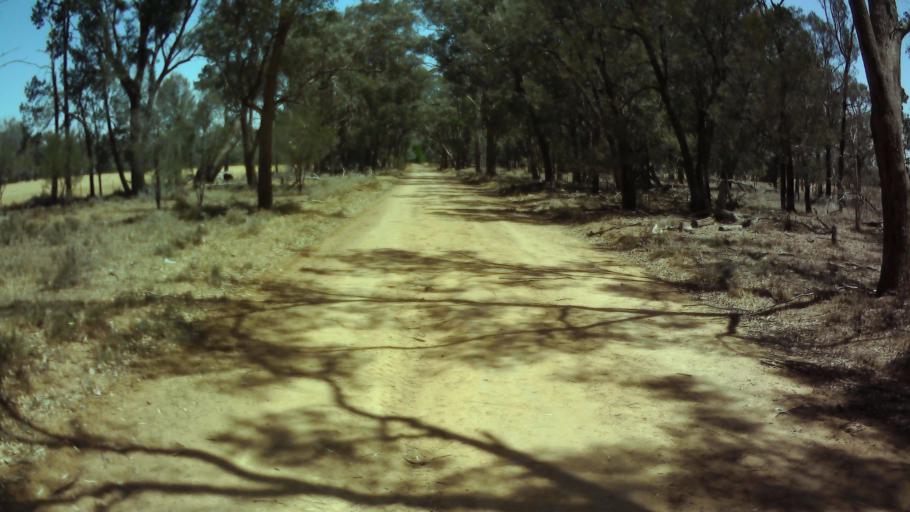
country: AU
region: New South Wales
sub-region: Weddin
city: Grenfell
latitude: -34.0442
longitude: 147.8405
